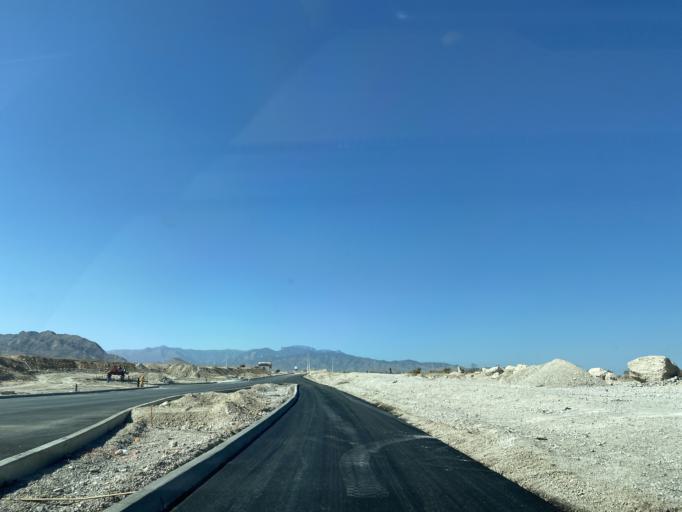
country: US
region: Nevada
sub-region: Clark County
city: Summerlin South
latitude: 36.3215
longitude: -115.3162
